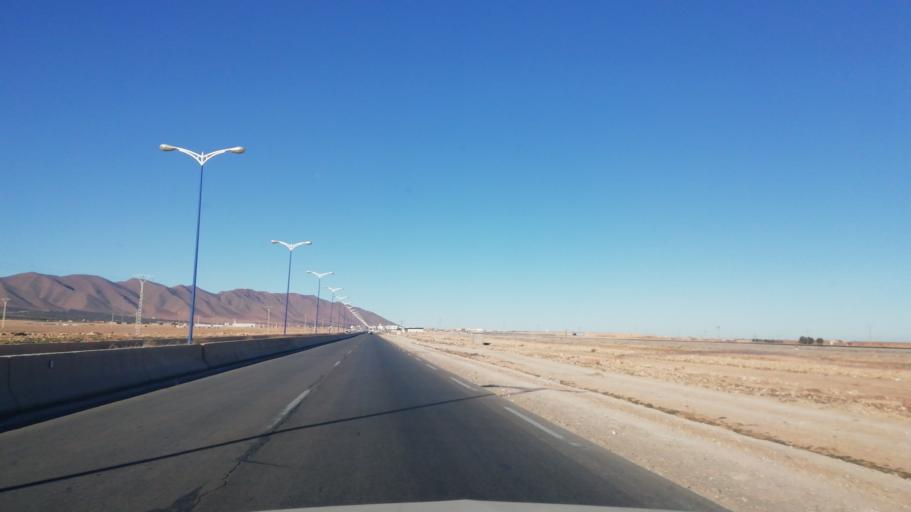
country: DZ
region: Wilaya de Naama
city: Naama
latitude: 33.4984
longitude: -0.2883
